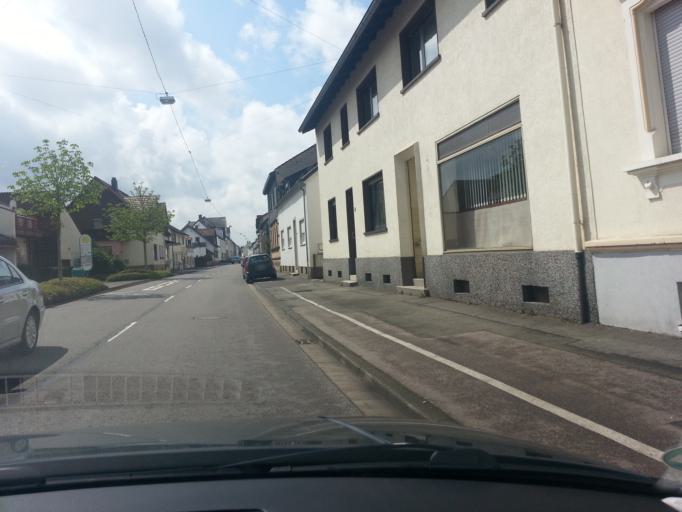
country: DE
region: Saarland
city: Homburg
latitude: 49.3101
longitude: 7.3167
